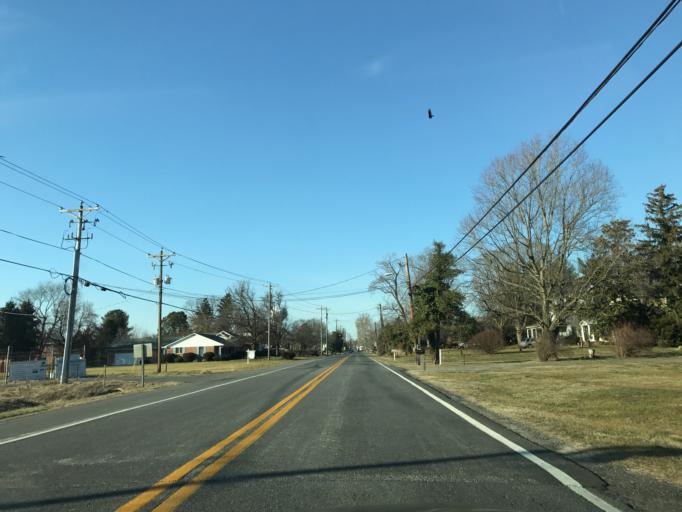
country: US
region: Maryland
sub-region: Queen Anne's County
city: Kingstown
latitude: 39.1808
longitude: -75.8577
